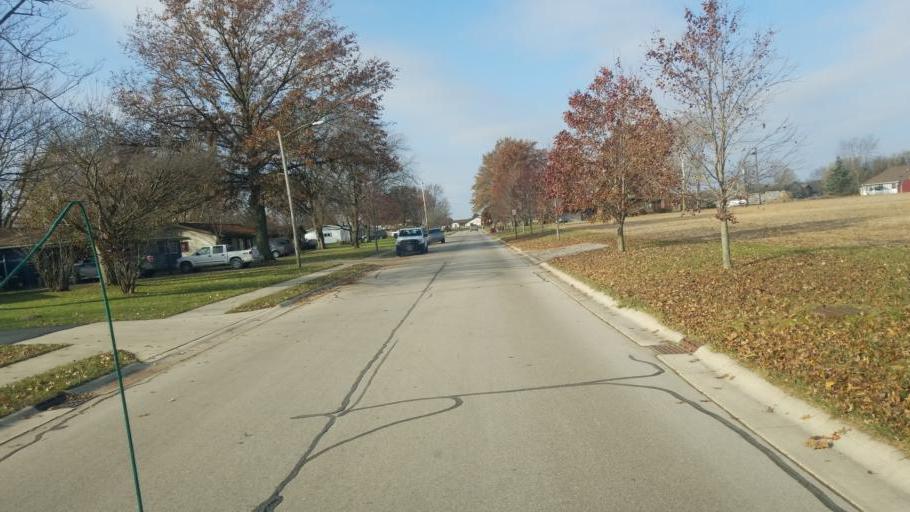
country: US
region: Indiana
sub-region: Adams County
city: Berne
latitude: 40.6594
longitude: -84.9612
